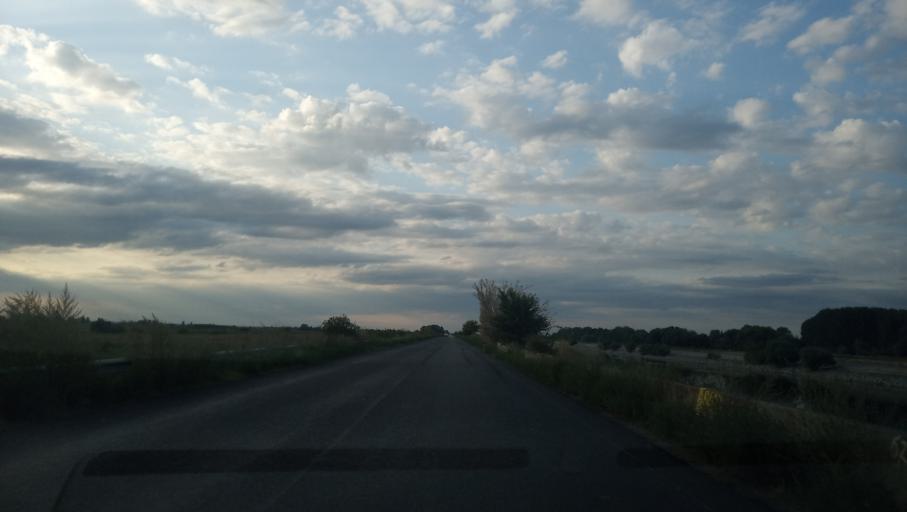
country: RO
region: Calarasi
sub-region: Municipiul Calarasi
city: Calarasi
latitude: 44.1755
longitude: 27.3081
